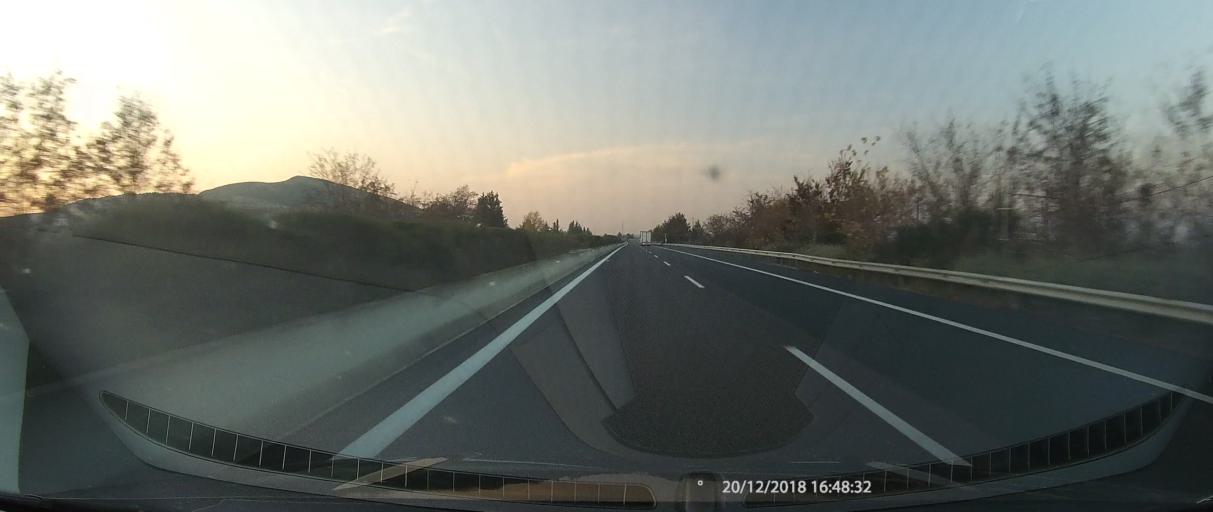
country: GR
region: Thessaly
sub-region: Nomos Magnisias
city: Stefanoviki
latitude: 39.4878
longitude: 22.6383
